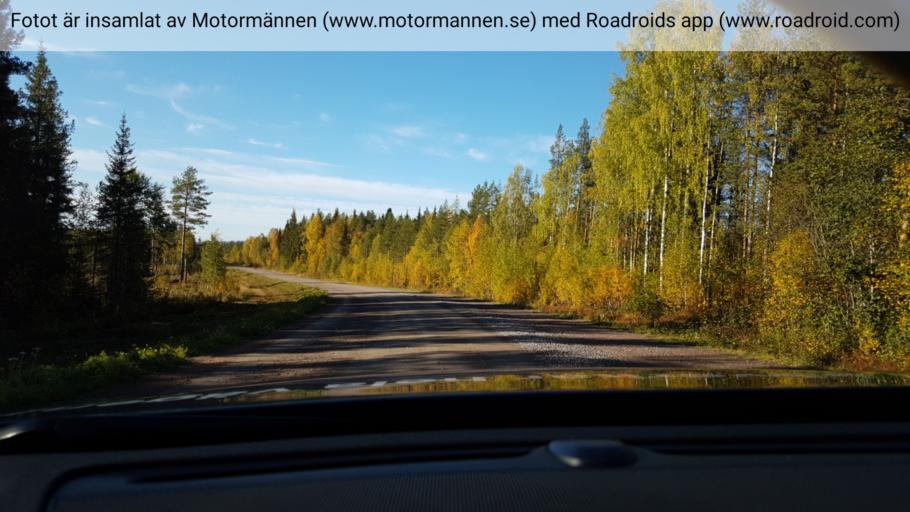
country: SE
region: Norrbotten
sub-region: Alvsbyns Kommun
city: AElvsbyn
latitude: 66.2577
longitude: 20.9446
